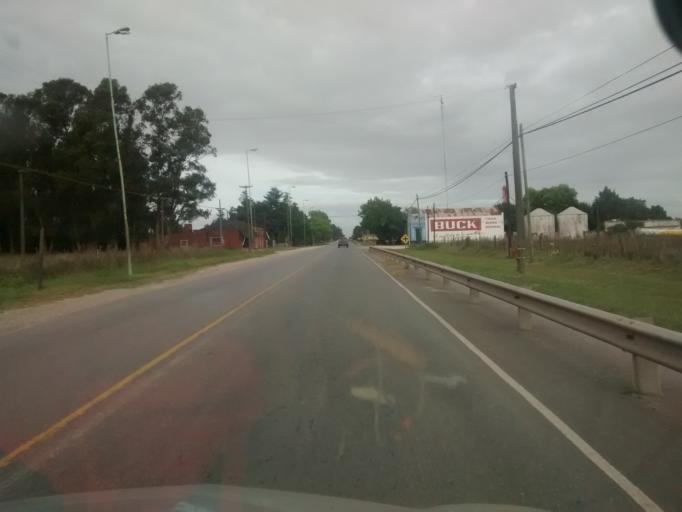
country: AR
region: Buenos Aires
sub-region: Partido de Loberia
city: Loberia
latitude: -38.1943
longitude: -58.7427
